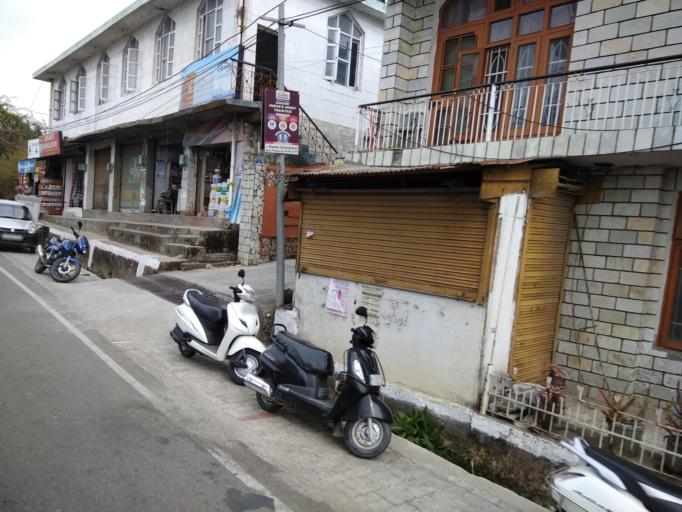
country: IN
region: Himachal Pradesh
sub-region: Kangra
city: Dharmsala
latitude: 32.2018
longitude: 76.3335
